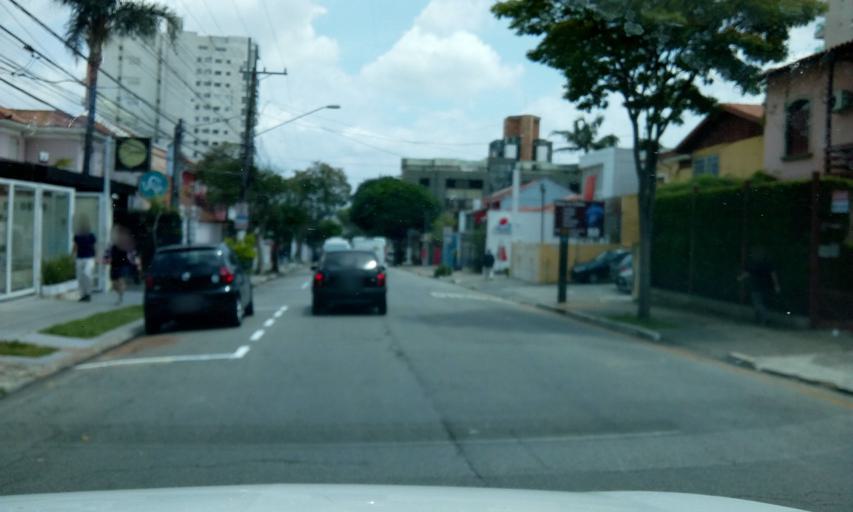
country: BR
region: Sao Paulo
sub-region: Sao Paulo
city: Sao Paulo
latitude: -23.5877
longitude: -46.6456
